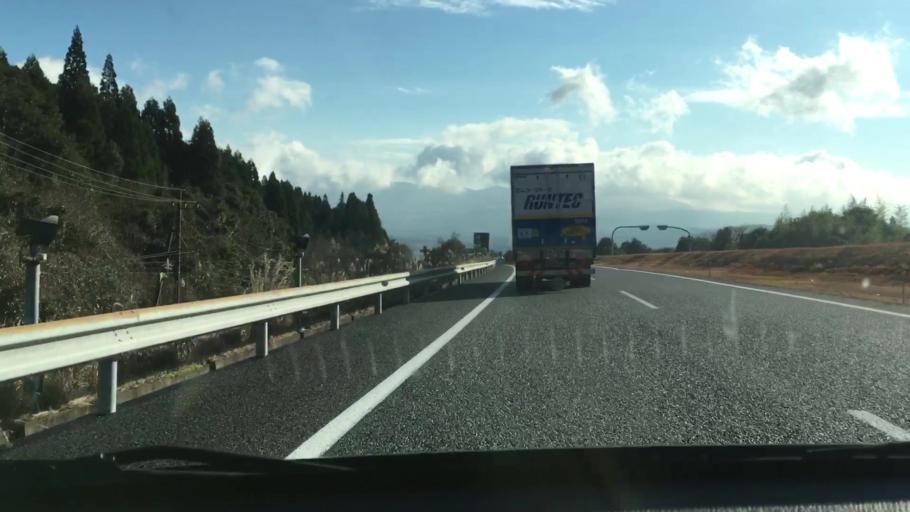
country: JP
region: Kumamoto
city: Hitoyoshi
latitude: 32.0765
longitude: 130.7929
